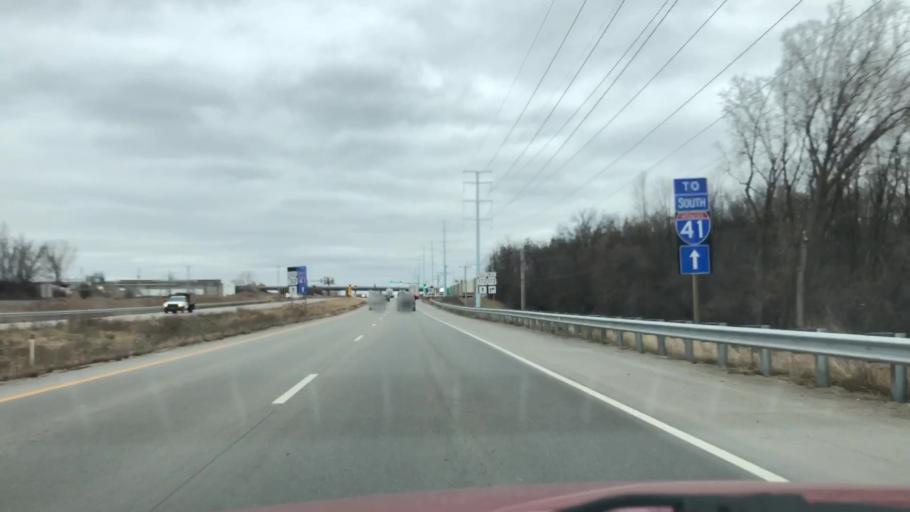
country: US
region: Wisconsin
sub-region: Brown County
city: Ashwaubenon
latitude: 44.4827
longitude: -88.0562
